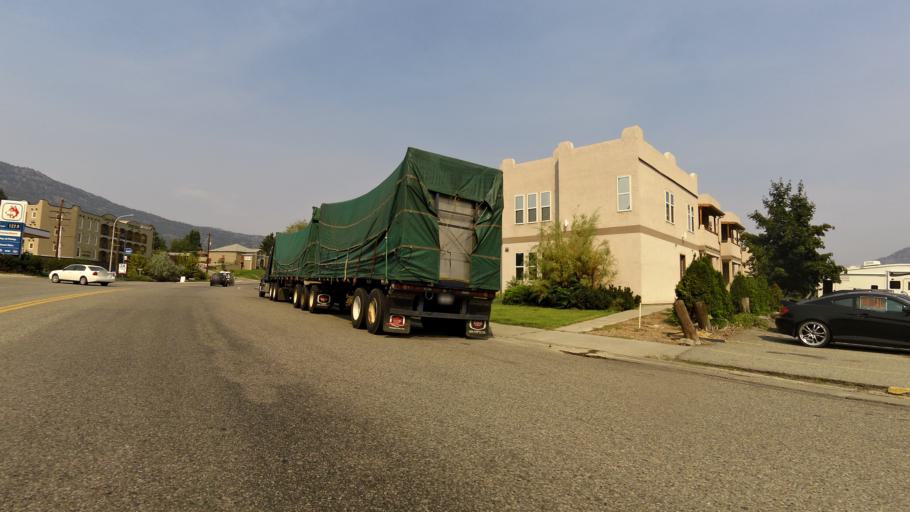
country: CA
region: British Columbia
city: Osoyoos
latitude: 49.0327
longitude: -119.4702
